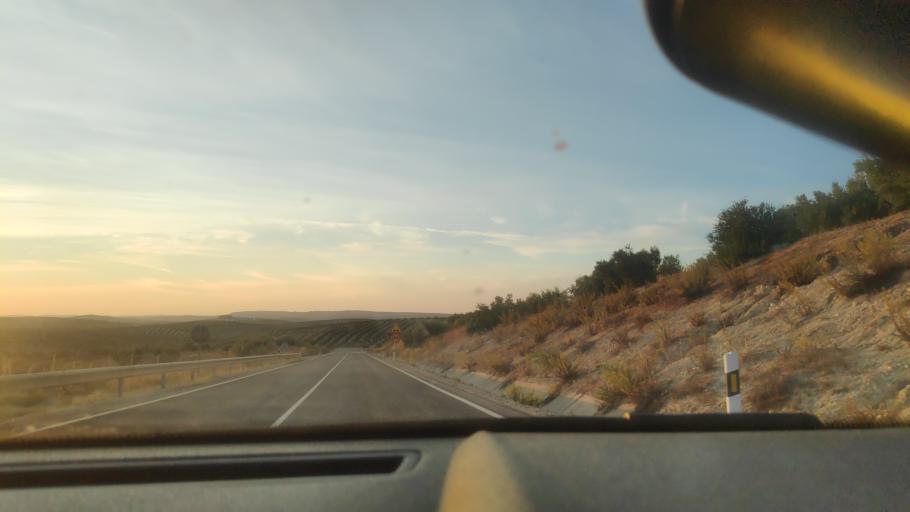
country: ES
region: Andalusia
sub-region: Provincia de Jaen
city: Villardompardo
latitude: 37.8265
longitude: -4.0447
